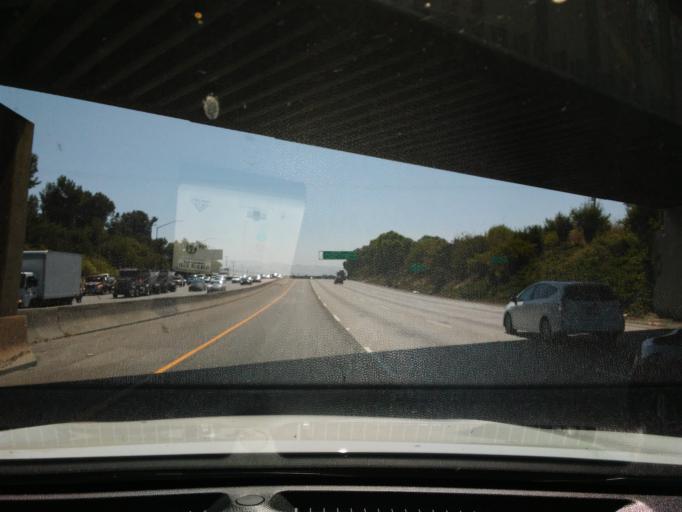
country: US
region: California
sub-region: Santa Clara County
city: Santa Clara
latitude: 37.3779
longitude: -121.9477
